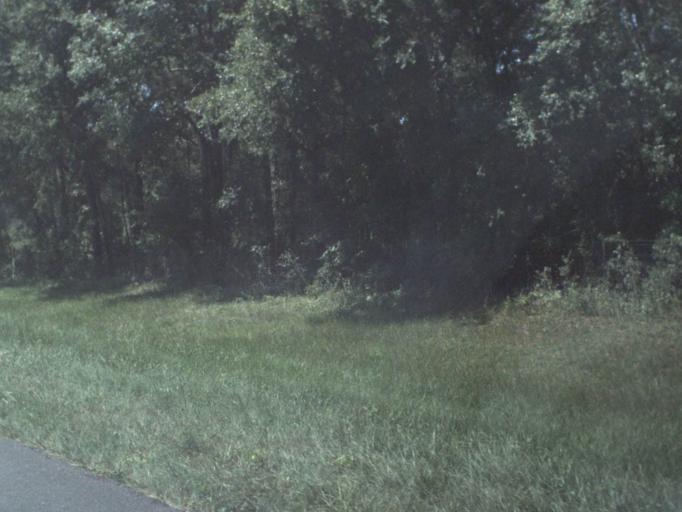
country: US
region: Florida
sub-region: Lafayette County
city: Mayo
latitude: 30.0925
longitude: -83.2310
